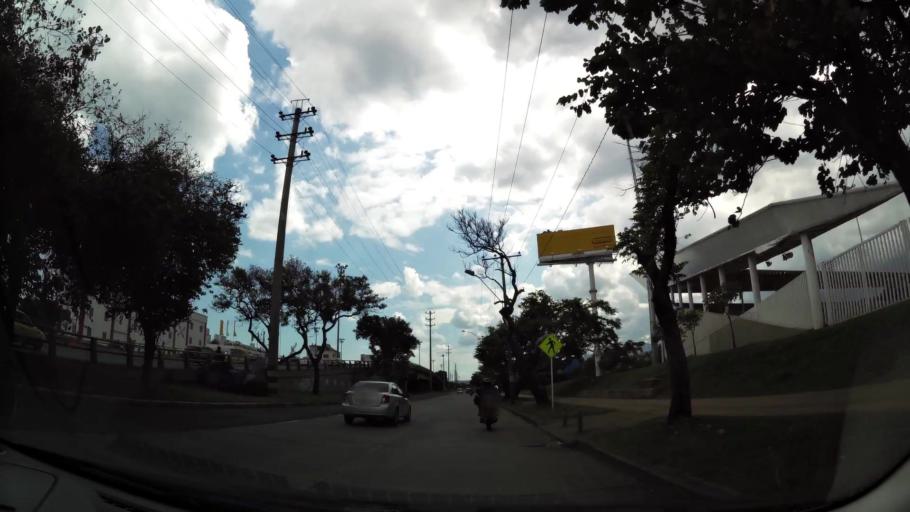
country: CO
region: Valle del Cauca
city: Cali
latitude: 3.4220
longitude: -76.5351
